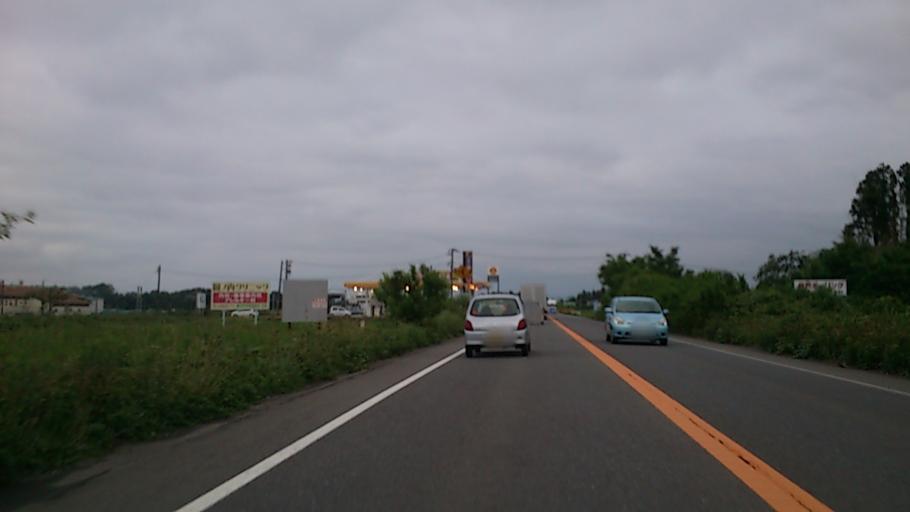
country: JP
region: Fukushima
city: Sukagawa
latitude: 37.2302
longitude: 140.3313
